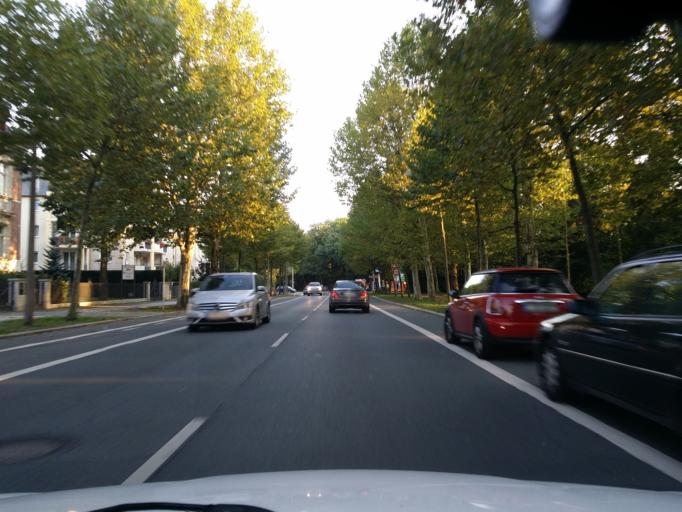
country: DE
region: Saxony
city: Leipzig
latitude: 51.3280
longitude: 12.3640
